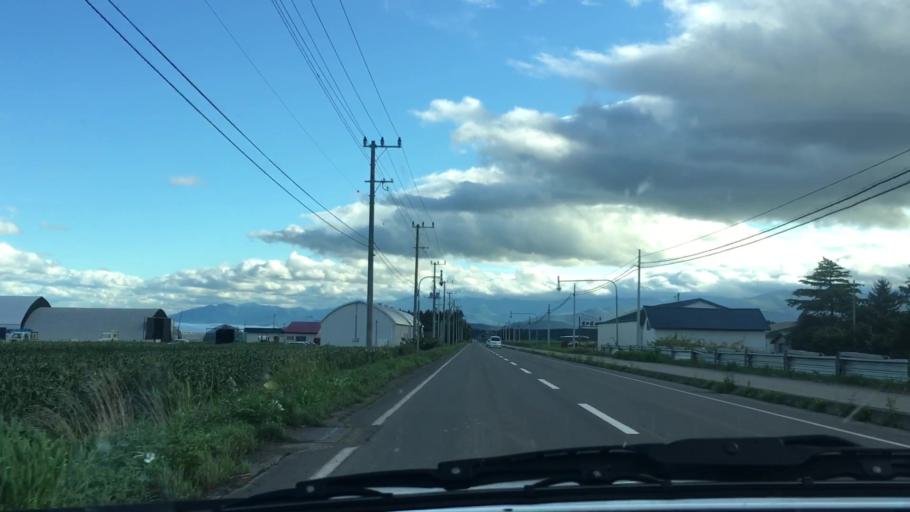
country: JP
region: Hokkaido
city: Otofuke
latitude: 43.1482
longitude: 142.8990
